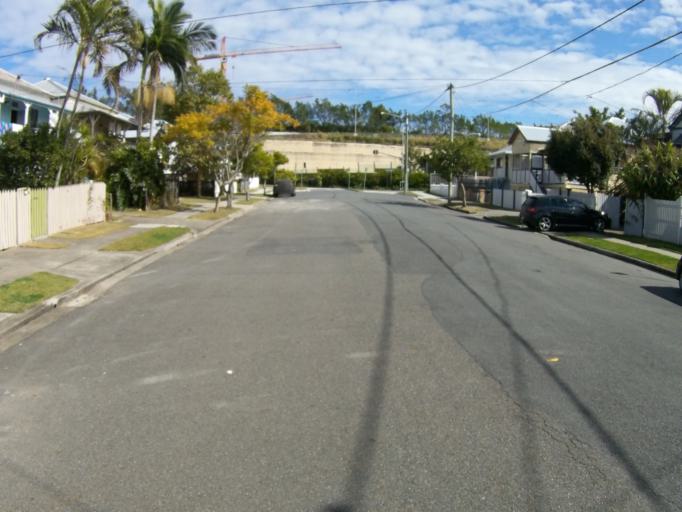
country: AU
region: Queensland
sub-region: Brisbane
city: Woolloongabba
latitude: -27.4989
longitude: 153.0412
